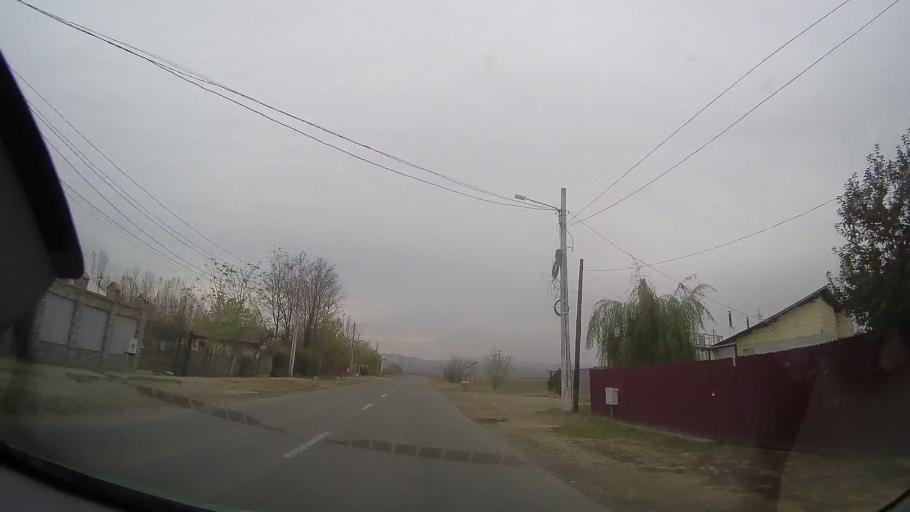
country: RO
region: Prahova
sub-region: Oras Urlati
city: Urlati
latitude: 44.9627
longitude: 26.2336
